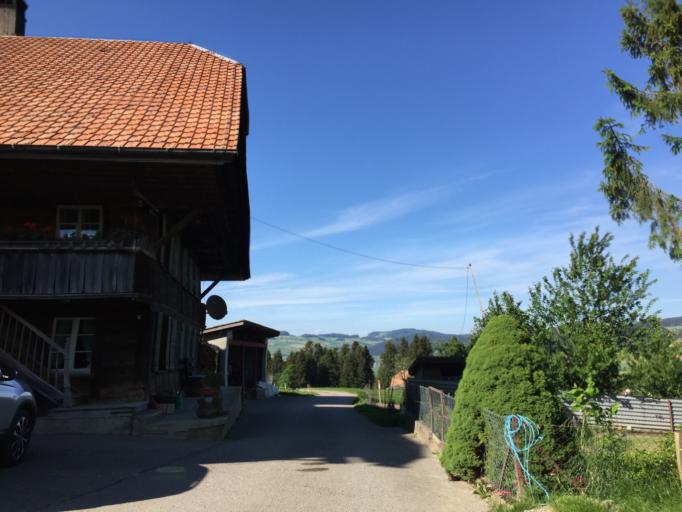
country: CH
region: Bern
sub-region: Bern-Mittelland District
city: Konolfingen
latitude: 46.8629
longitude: 7.6168
